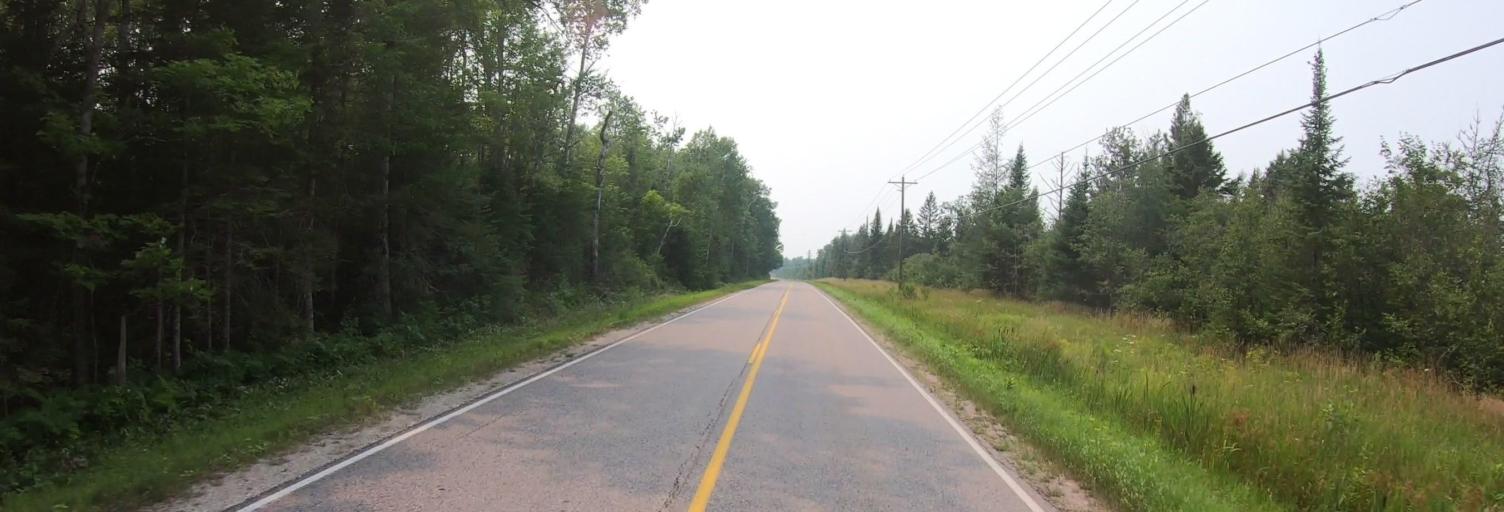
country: CA
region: Ontario
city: Thessalon
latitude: 46.0148
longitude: -84.0252
